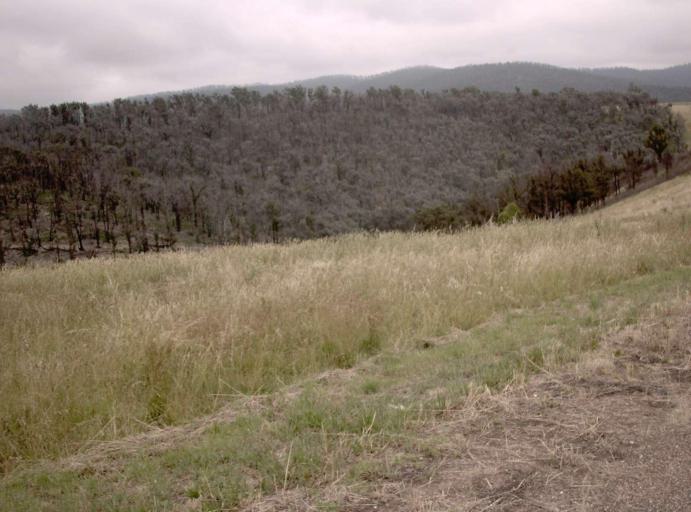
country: AU
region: Victoria
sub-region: Wellington
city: Heyfield
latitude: -37.8437
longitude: 146.6937
